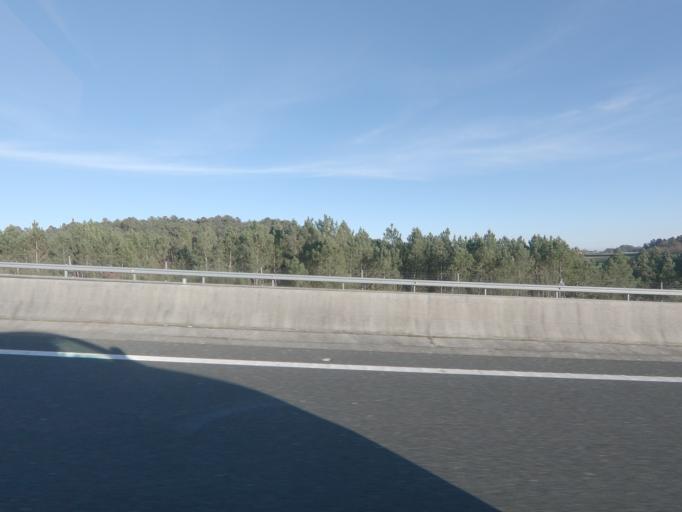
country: ES
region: Galicia
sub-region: Provincia de Ourense
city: Pinor
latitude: 42.5312
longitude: -8.0155
